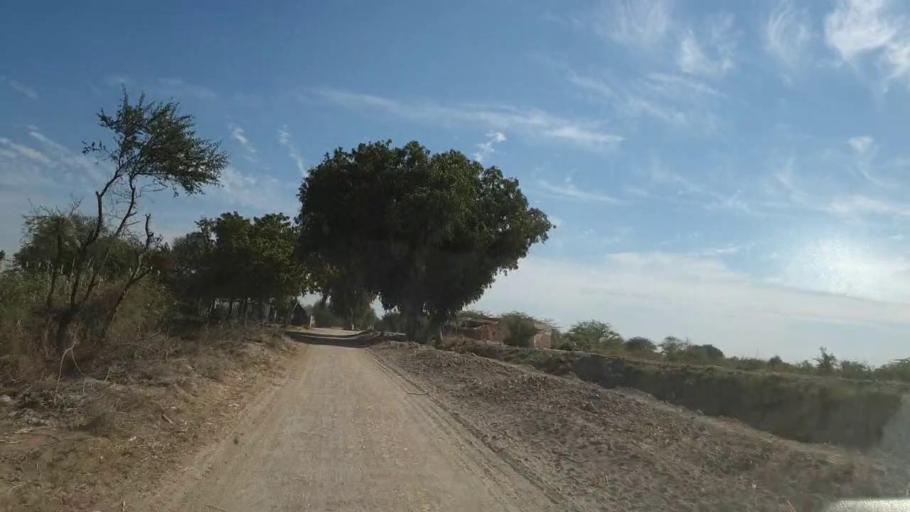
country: PK
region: Sindh
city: Pithoro
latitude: 25.5387
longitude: 69.3026
